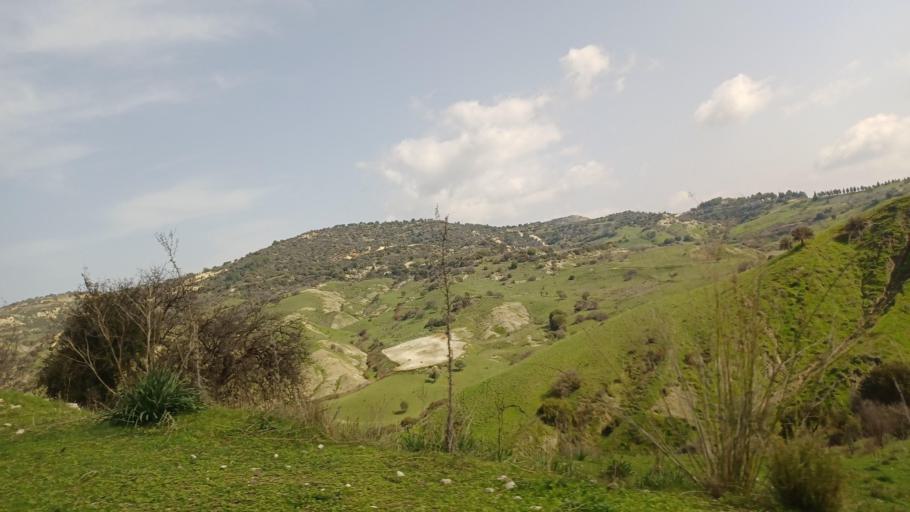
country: CY
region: Limassol
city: Pissouri
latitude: 34.7500
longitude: 32.6596
